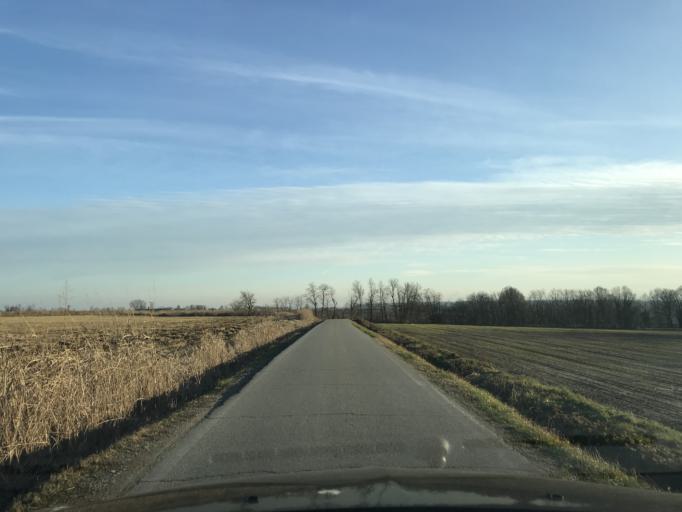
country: IT
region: Lombardy
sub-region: Provincia di Lodi
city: Bargano
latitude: 45.2311
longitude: 9.4545
